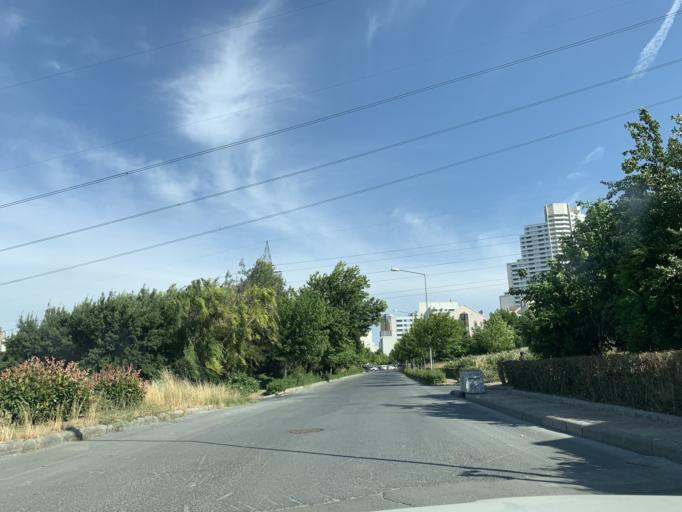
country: TR
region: Istanbul
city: Esenyurt
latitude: 41.0817
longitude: 28.6751
